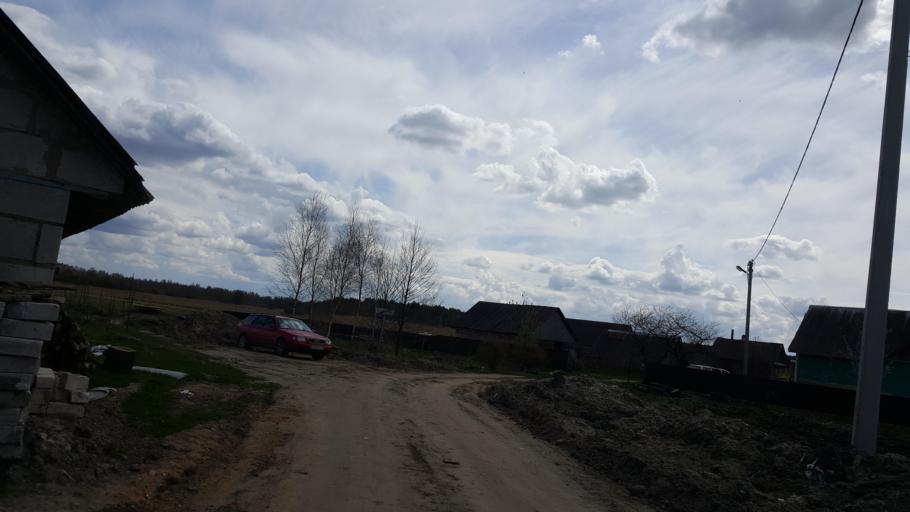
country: BY
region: Brest
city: Kamyanyets
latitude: 52.3496
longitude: 23.7304
